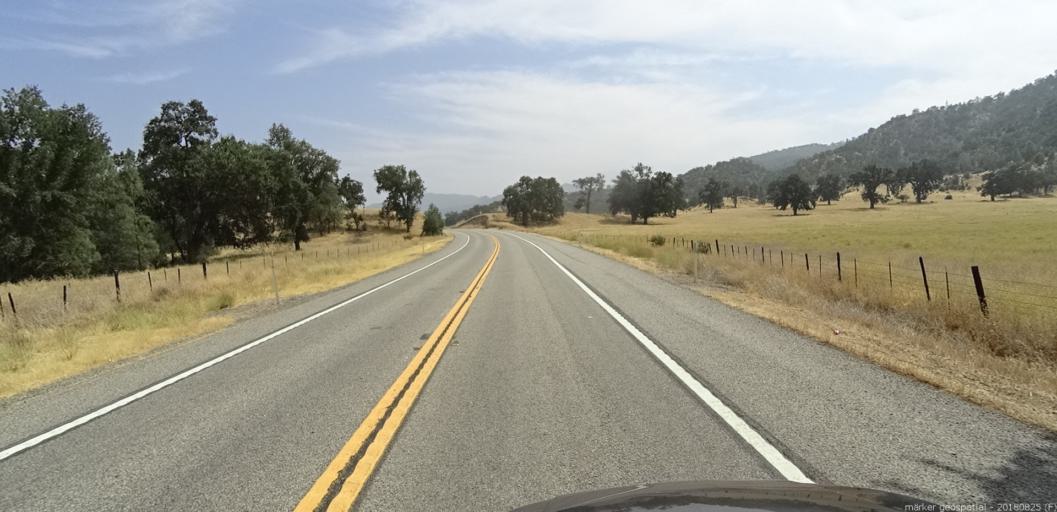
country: US
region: California
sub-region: Fresno County
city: Coalinga
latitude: 36.1884
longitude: -120.7059
